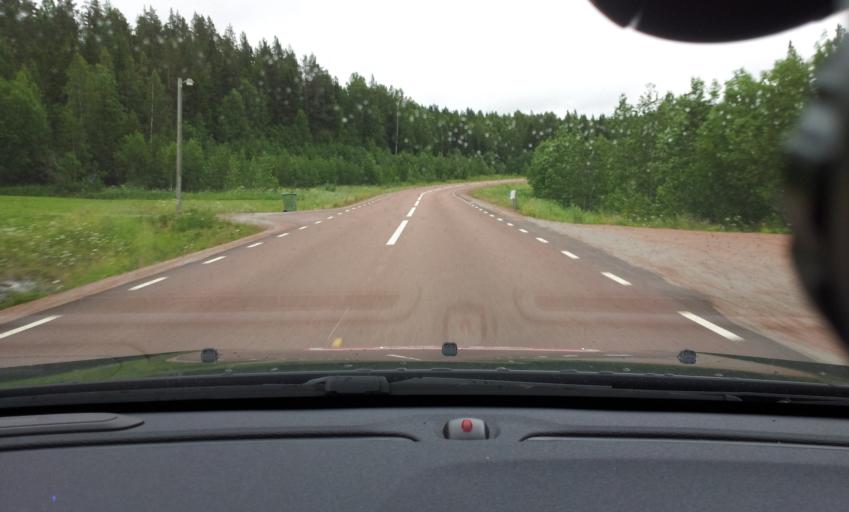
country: SE
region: Jaemtland
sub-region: Ragunda Kommun
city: Hammarstrand
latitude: 63.0518
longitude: 16.4934
